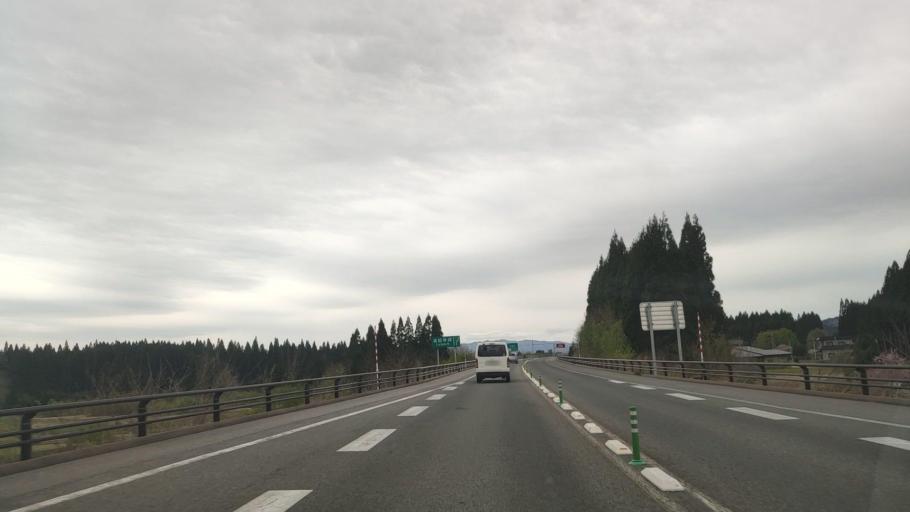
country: JP
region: Akita
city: Odate
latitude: 40.3092
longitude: 140.5755
